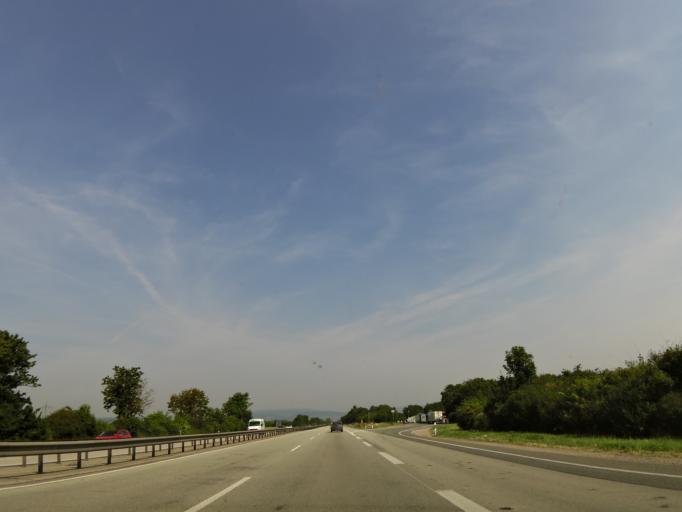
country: DE
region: Rheinland-Pfalz
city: Zotzenheim
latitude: 49.8741
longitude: 7.9570
